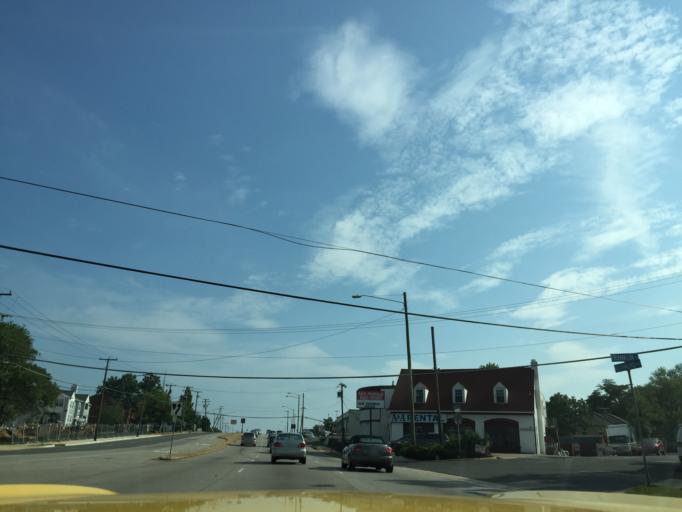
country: US
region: Virginia
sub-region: Fairfax County
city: Groveton
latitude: 38.7783
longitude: -77.0800
